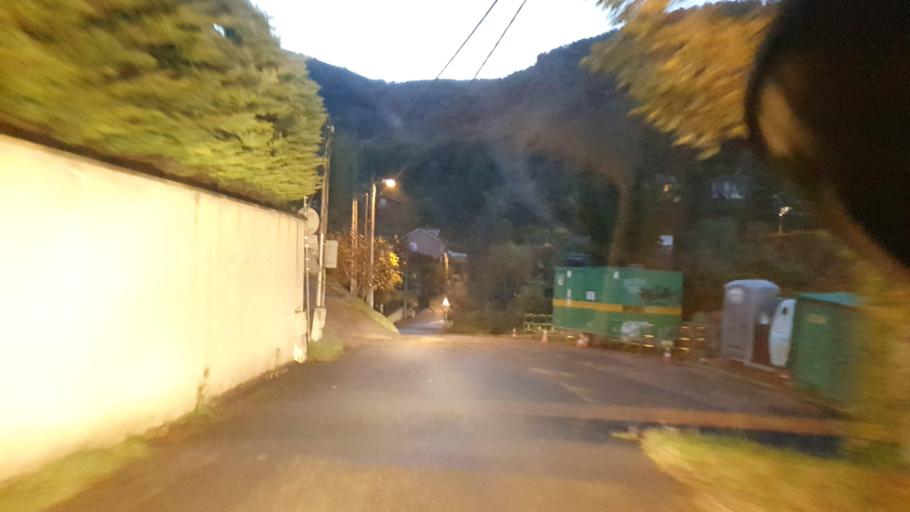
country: FR
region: Rhone-Alpes
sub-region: Departement du Rhone
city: Albigny-sur-Saone
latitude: 45.8439
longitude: 4.8199
